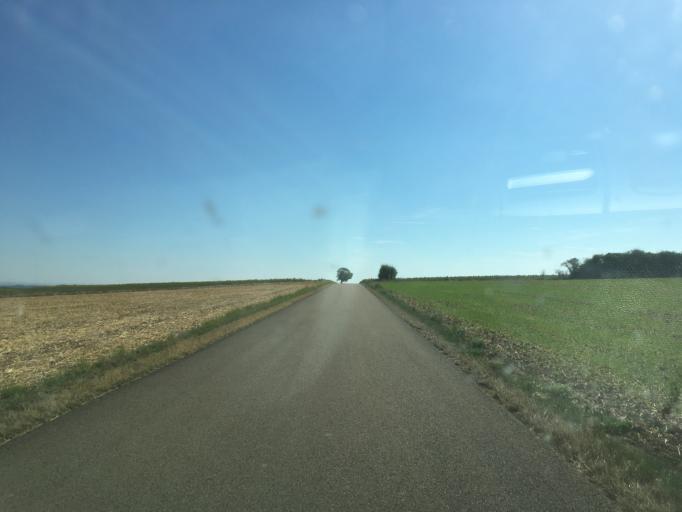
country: FR
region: Bourgogne
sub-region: Departement de l'Yonne
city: Joigny
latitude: 47.9187
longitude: 3.4007
